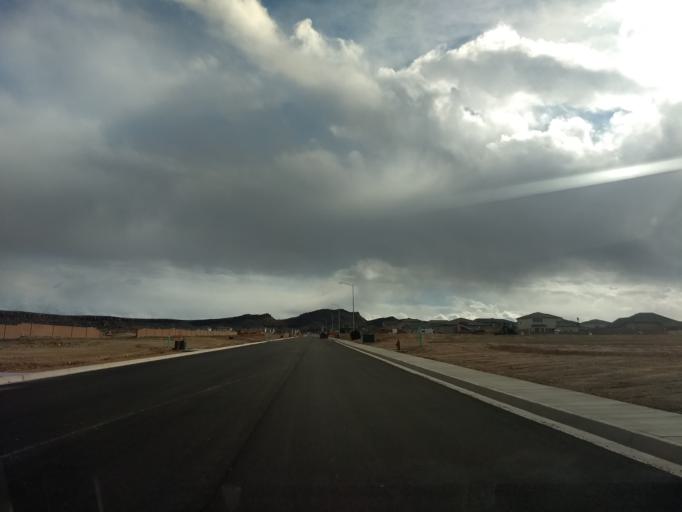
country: US
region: Utah
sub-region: Washington County
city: Washington
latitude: 37.0624
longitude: -113.5177
